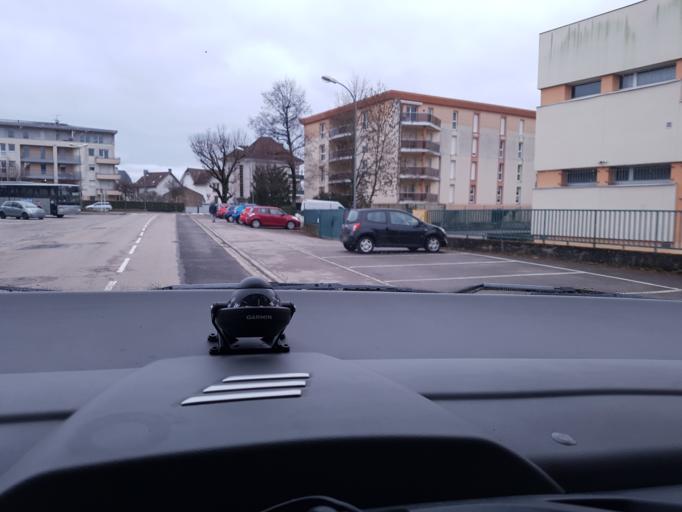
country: FR
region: Lorraine
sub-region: Departement des Vosges
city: Saint-Die-des-Vosges
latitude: 48.2863
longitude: 6.9554
